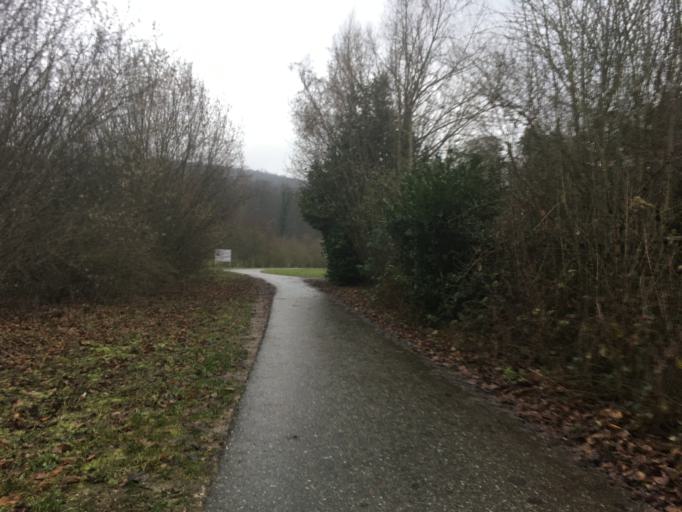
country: DE
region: Baden-Wuerttemberg
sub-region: Karlsruhe Region
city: Ettlingen
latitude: 48.9700
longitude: 8.4459
